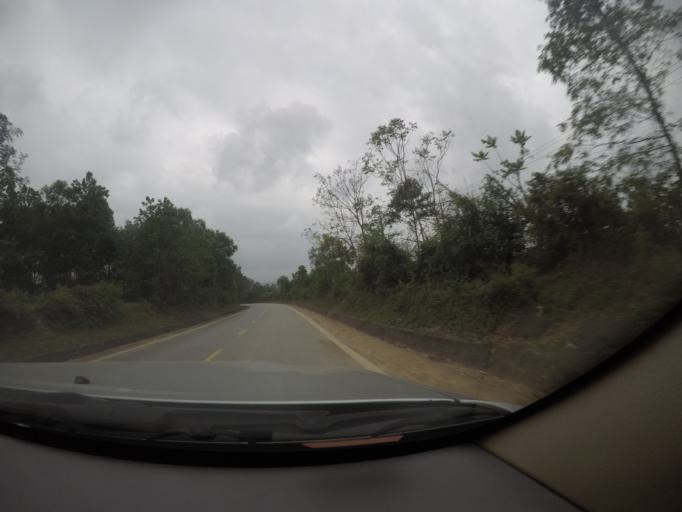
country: VN
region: Quang Tri
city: Cam Lo
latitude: 16.8345
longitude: 107.0003
